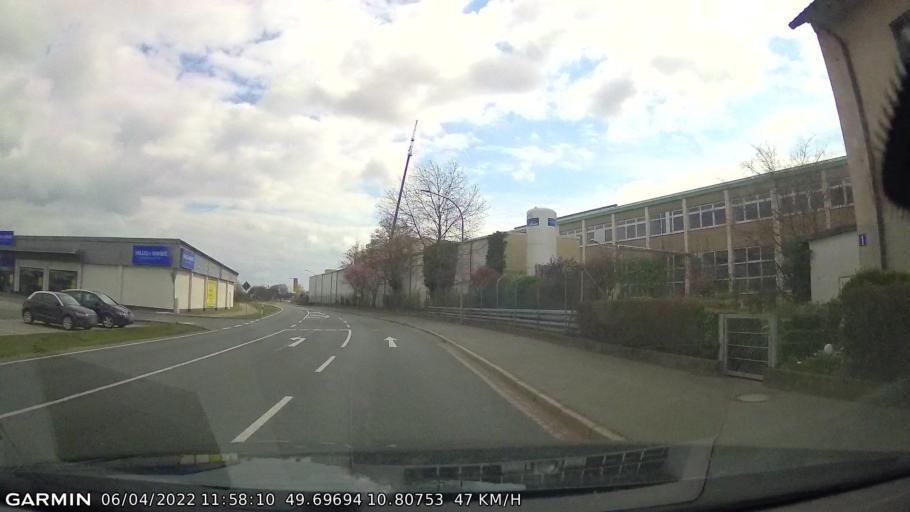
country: DE
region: Bavaria
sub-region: Regierungsbezirk Mittelfranken
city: Hochstadt an der Aisch
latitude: 49.6970
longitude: 10.8075
